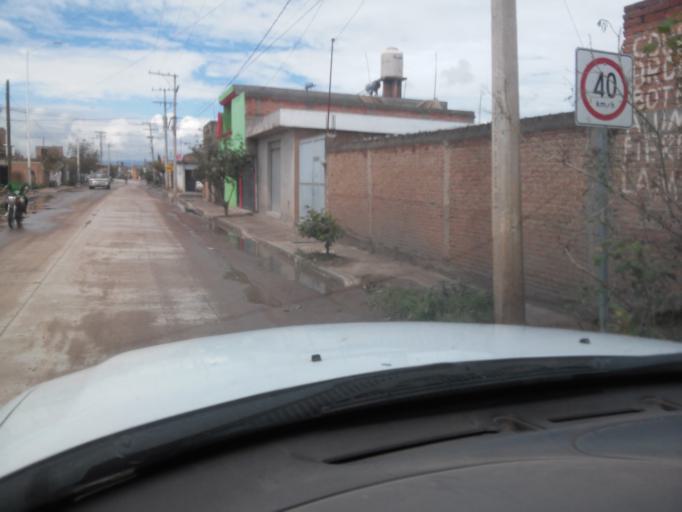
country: MX
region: Durango
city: Victoria de Durango
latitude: 24.0179
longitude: -104.6119
